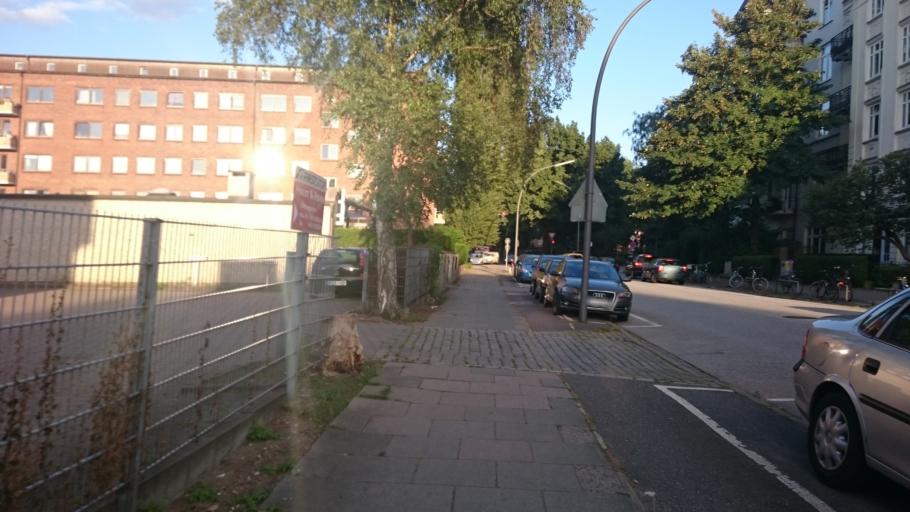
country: DE
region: Hamburg
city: St. Pauli
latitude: 53.5816
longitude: 9.9551
